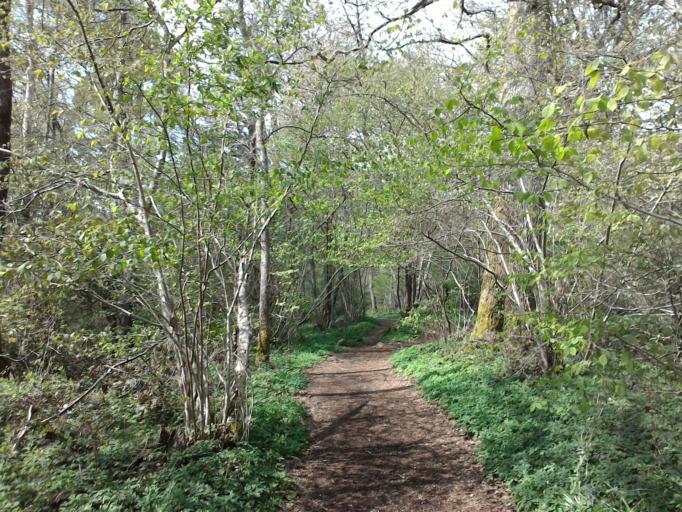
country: FR
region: Bourgogne
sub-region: Departement de la Cote-d'Or
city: Saulieu
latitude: 47.1819
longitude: 4.0771
